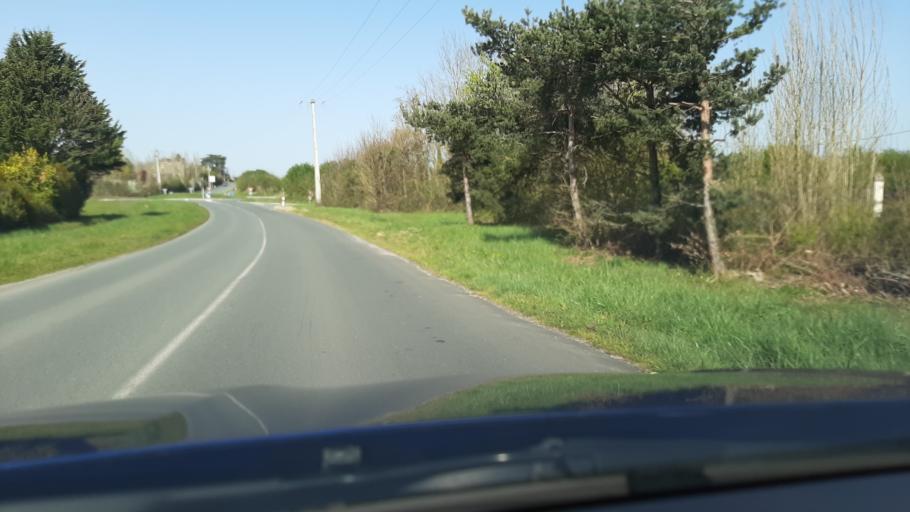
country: FR
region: Pays de la Loire
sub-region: Departement de Maine-et-Loire
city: Pellouailles-les-Vignes
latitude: 47.5102
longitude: -0.4487
